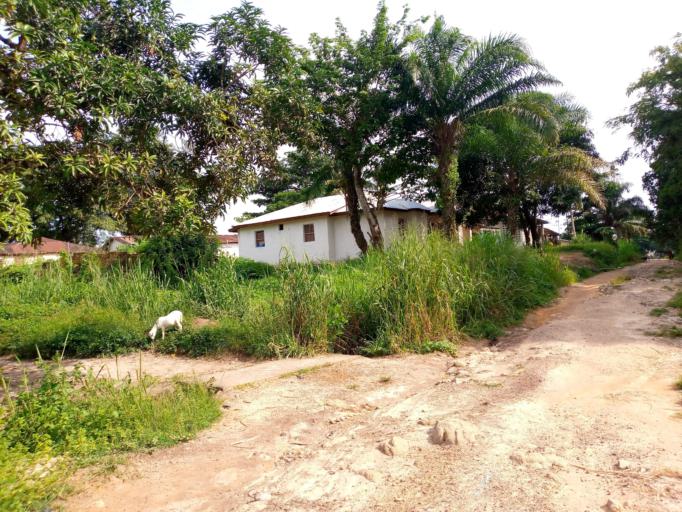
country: SL
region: Northern Province
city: Magburaka
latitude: 8.7249
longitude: -11.9462
